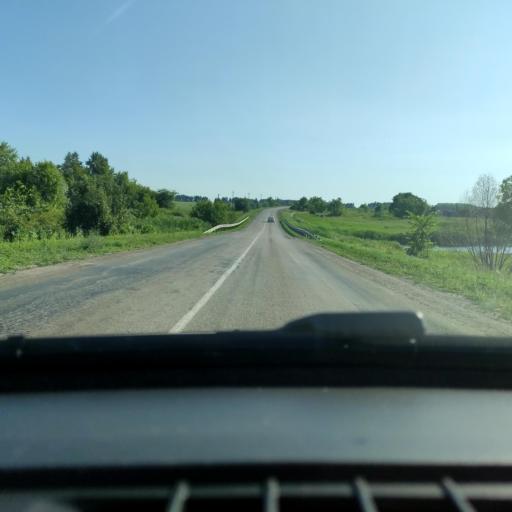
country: RU
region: Voronezj
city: Panino
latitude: 51.6116
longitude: 40.0052
